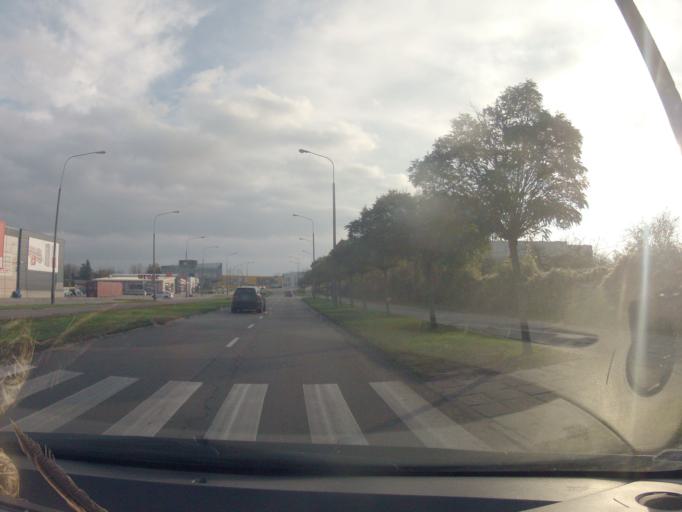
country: PL
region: Opole Voivodeship
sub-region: Powiat opolski
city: Opole
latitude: 50.6709
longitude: 17.9504
